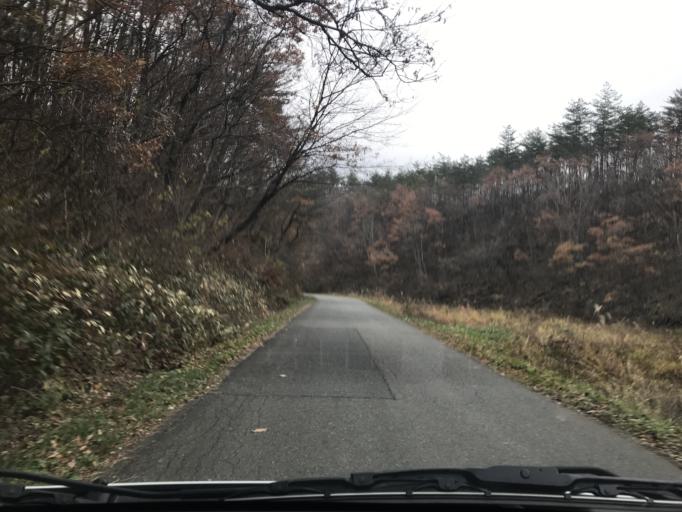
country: JP
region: Iwate
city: Ichinoseki
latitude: 39.0047
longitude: 141.0293
